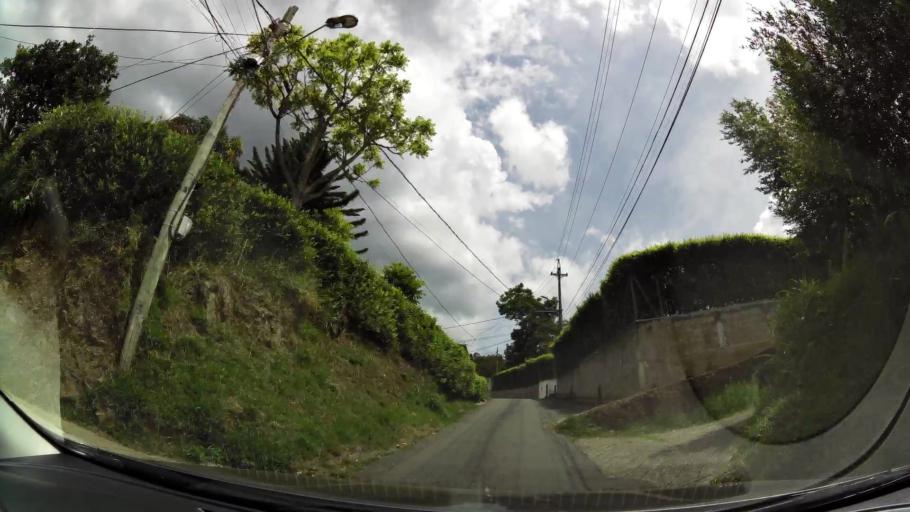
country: CO
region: Antioquia
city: Municipio de Copacabana
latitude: 6.3261
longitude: -75.4988
